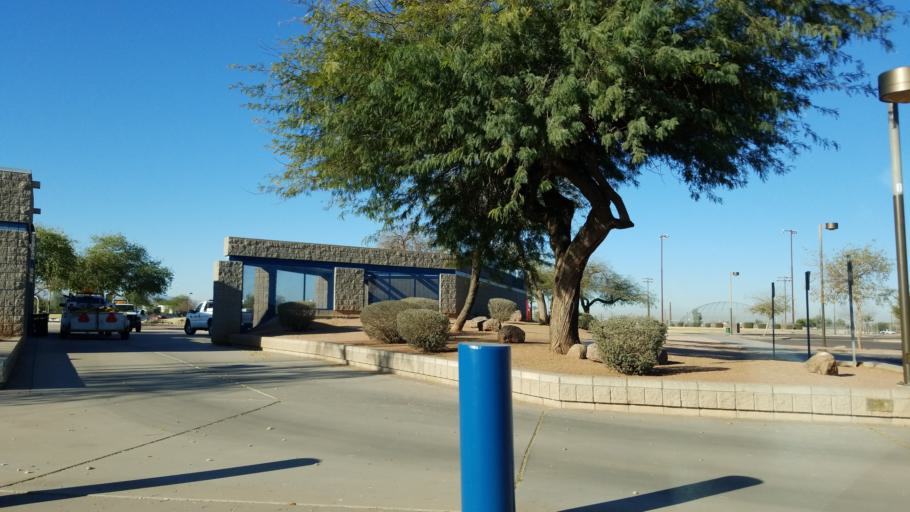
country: US
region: Arizona
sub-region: Maricopa County
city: Phoenix
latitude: 33.4303
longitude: -112.0494
